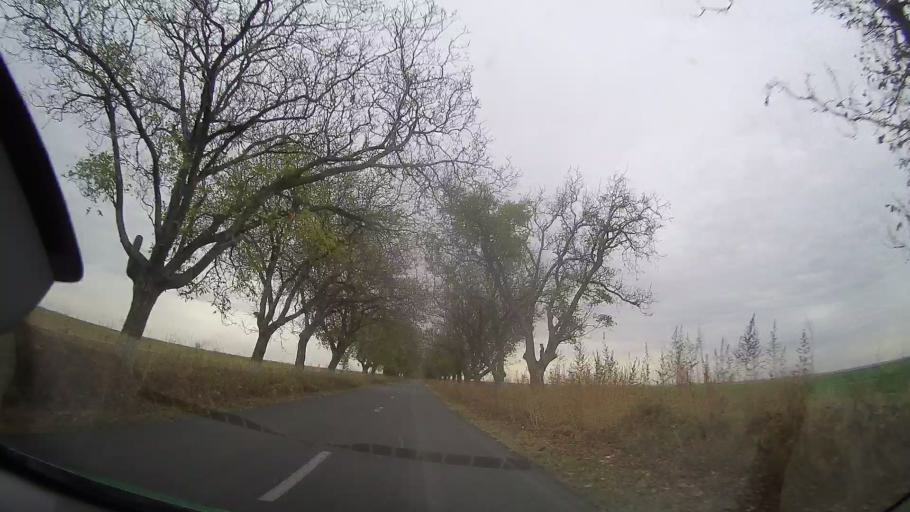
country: RO
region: Prahova
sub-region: Comuna Fantanele
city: Fantanele
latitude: 45.0184
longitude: 26.3976
